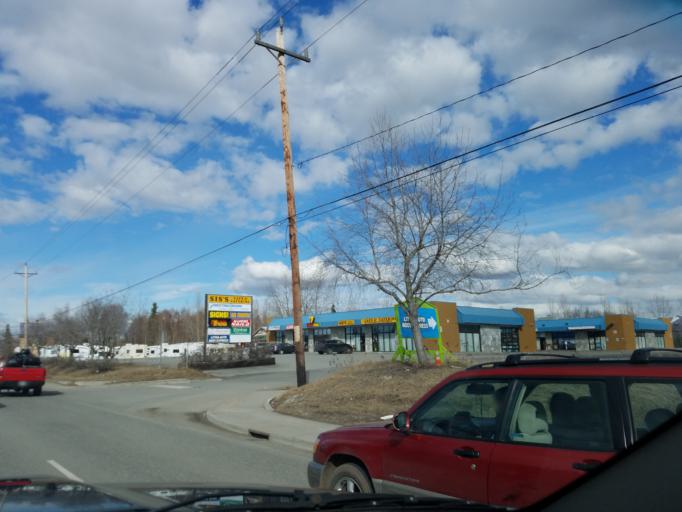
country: US
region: Alaska
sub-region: Anchorage Municipality
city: Anchorage
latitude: 61.1708
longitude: -149.8681
